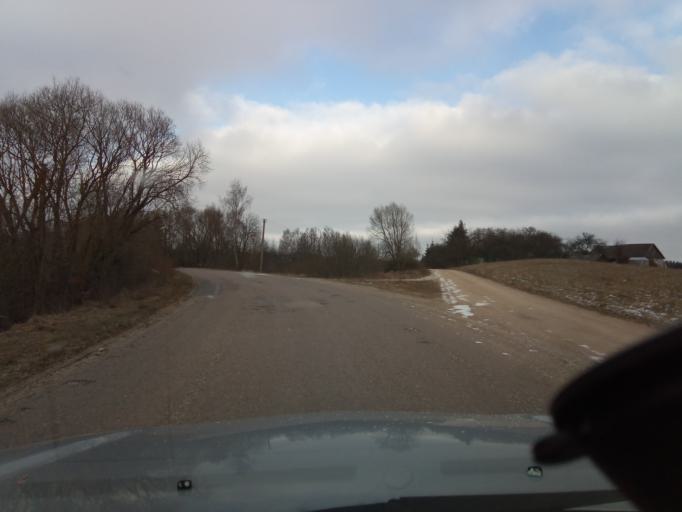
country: LT
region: Alytaus apskritis
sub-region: Alytaus rajonas
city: Daugai
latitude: 54.3527
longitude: 24.2612
